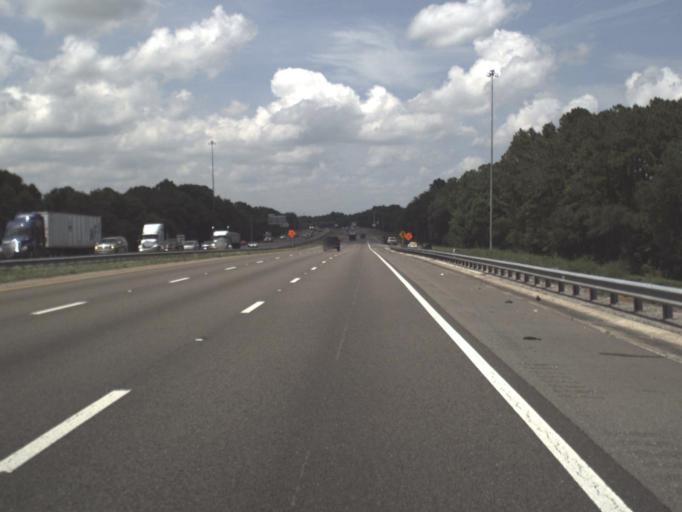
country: US
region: Florida
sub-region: Clay County
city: Bellair-Meadowbrook Terrace
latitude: 30.2488
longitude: -81.7627
